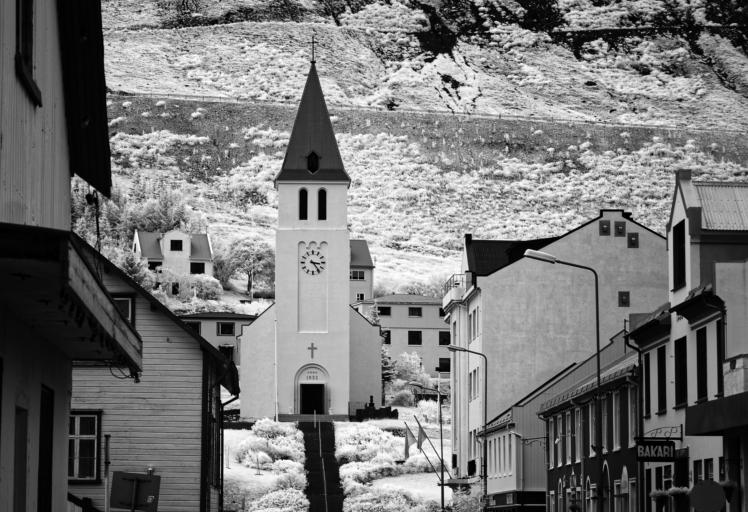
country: IS
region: Northeast
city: Siglufjoerdur
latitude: 66.1503
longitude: -18.9066
